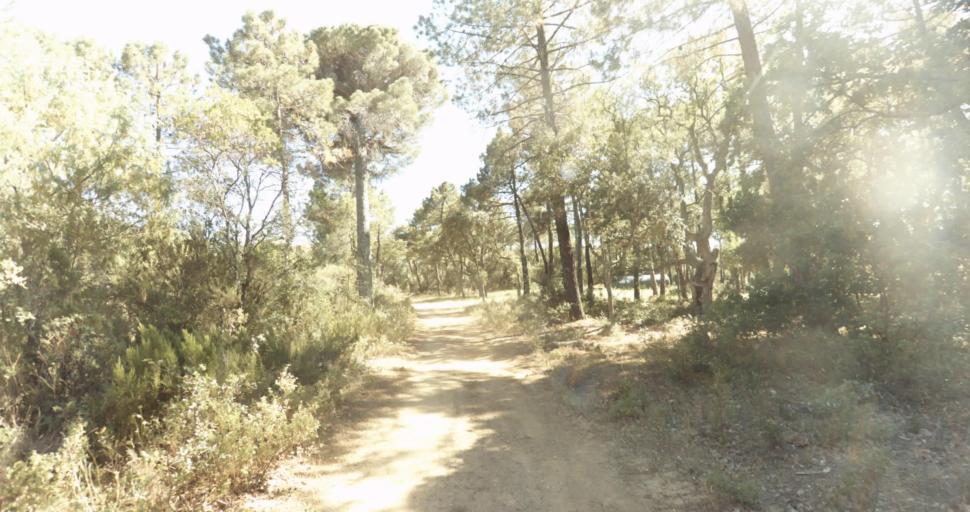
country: FR
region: Provence-Alpes-Cote d'Azur
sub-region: Departement du Var
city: Gassin
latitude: 43.2473
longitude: 6.5845
